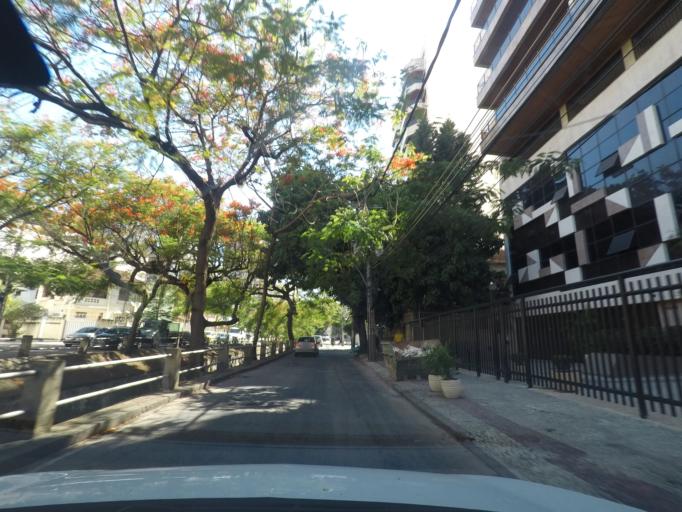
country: BR
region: Rio de Janeiro
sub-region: Rio De Janeiro
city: Rio de Janeiro
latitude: -22.9286
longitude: -43.2402
